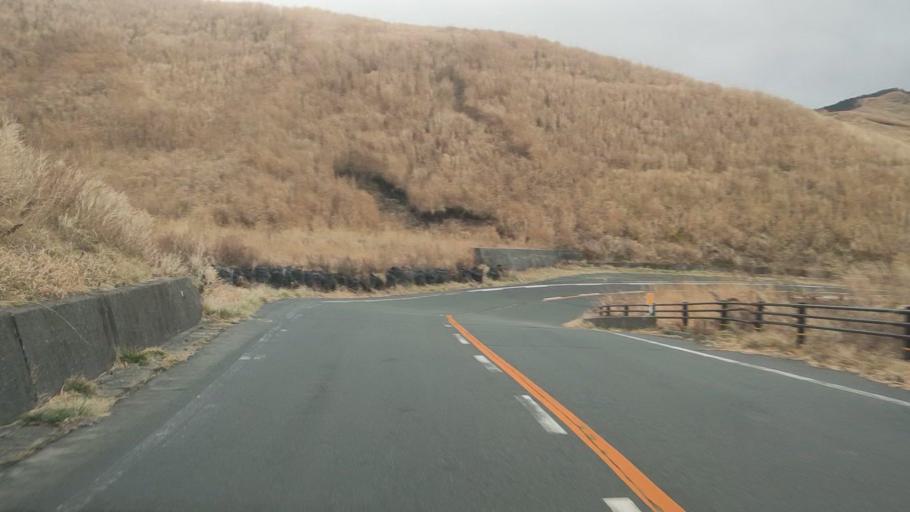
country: JP
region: Kumamoto
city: Aso
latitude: 32.9038
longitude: 131.1523
